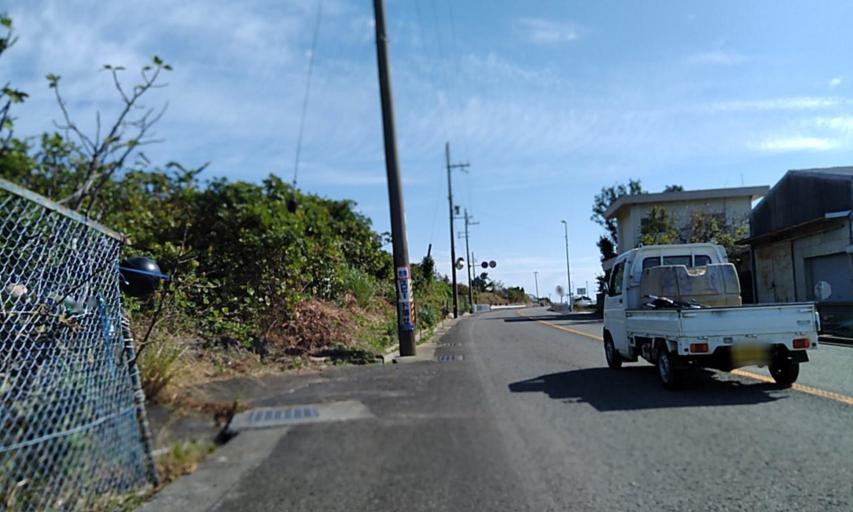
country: JP
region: Wakayama
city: Gobo
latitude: 33.8251
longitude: 135.1896
